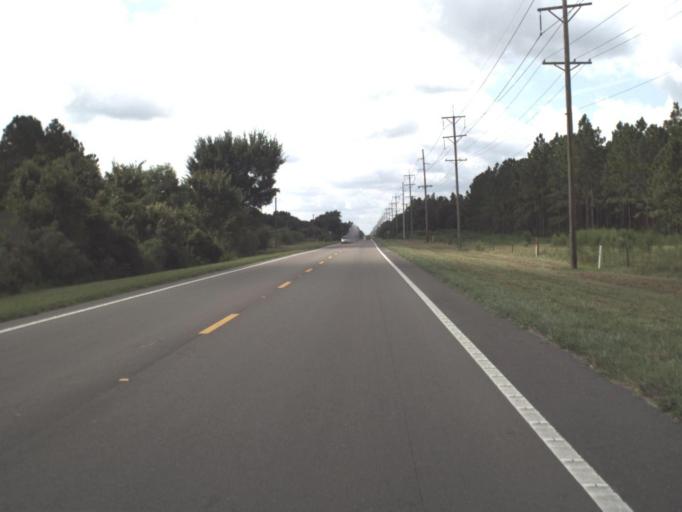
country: US
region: Florida
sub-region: Pasco County
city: Crystal Springs
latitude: 28.1599
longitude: -82.1538
